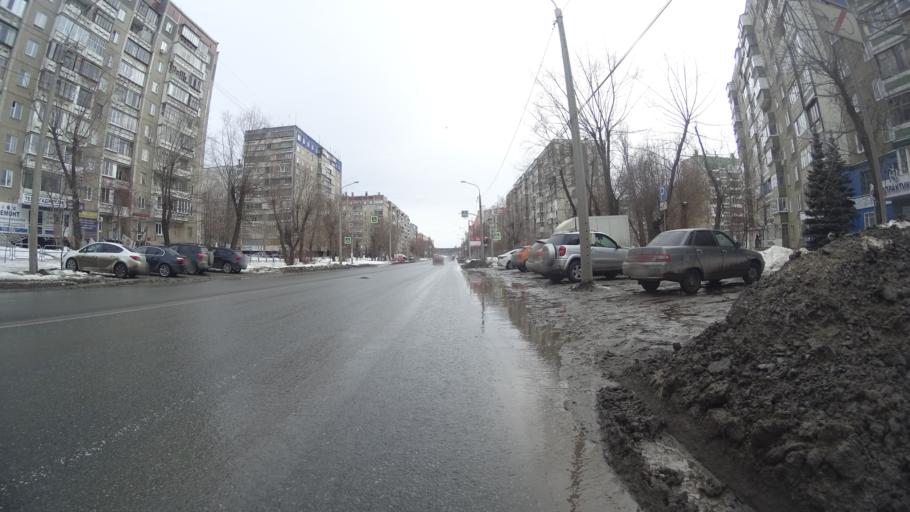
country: RU
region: Chelyabinsk
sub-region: Gorod Chelyabinsk
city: Chelyabinsk
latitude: 55.1799
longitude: 61.3071
